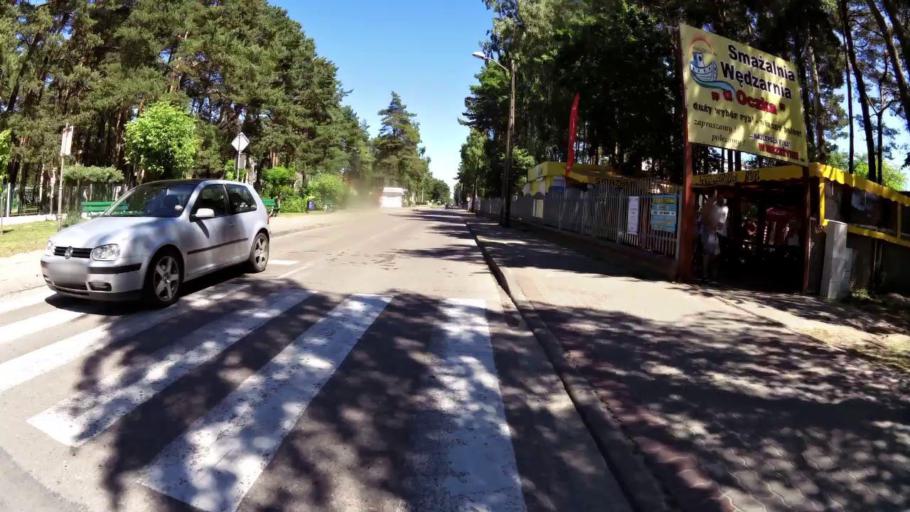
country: PL
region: West Pomeranian Voivodeship
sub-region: Powiat gryficki
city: Mrzezyno
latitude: 54.1447
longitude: 15.3026
